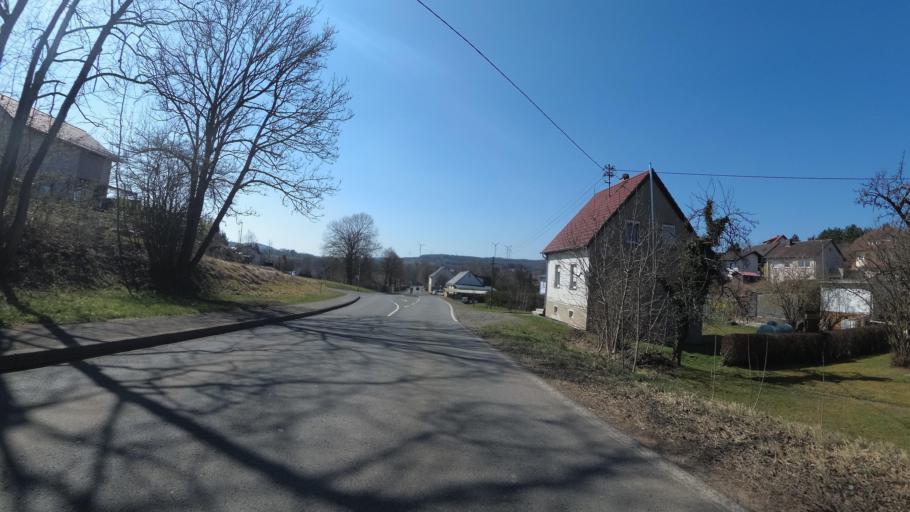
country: DE
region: Rheinland-Pfalz
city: Brucken
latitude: 49.6389
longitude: 7.1200
